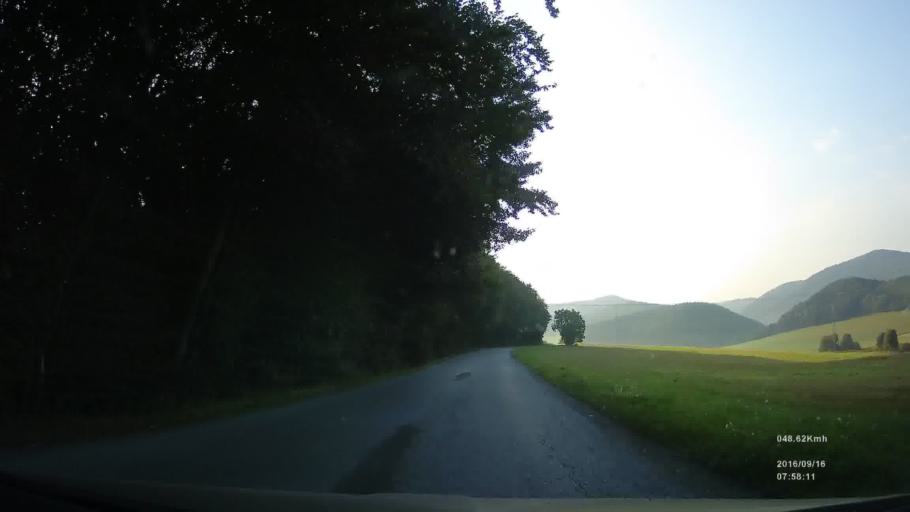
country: SK
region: Presovsky
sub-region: Okres Presov
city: Presov
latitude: 48.9108
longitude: 21.1514
